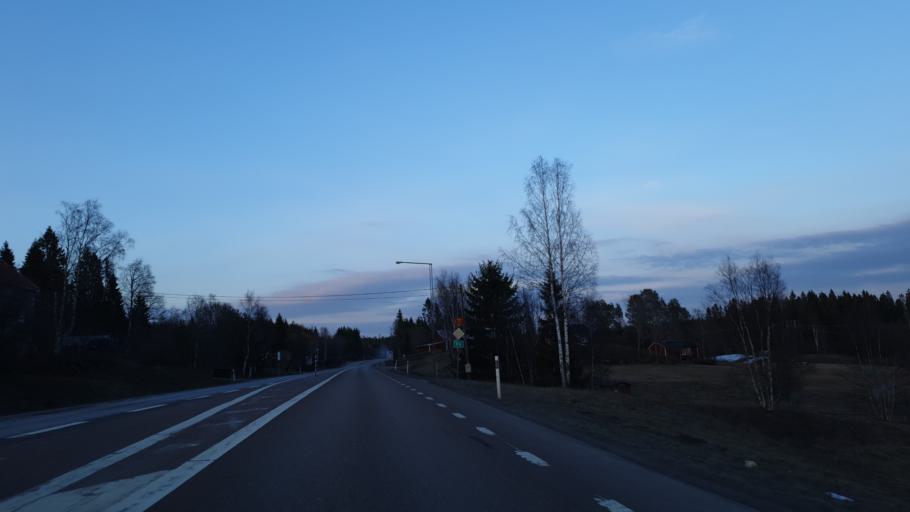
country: SE
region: Vaesternorrland
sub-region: Haernoesands Kommun
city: Haernoesand
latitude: 62.7066
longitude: 17.8682
